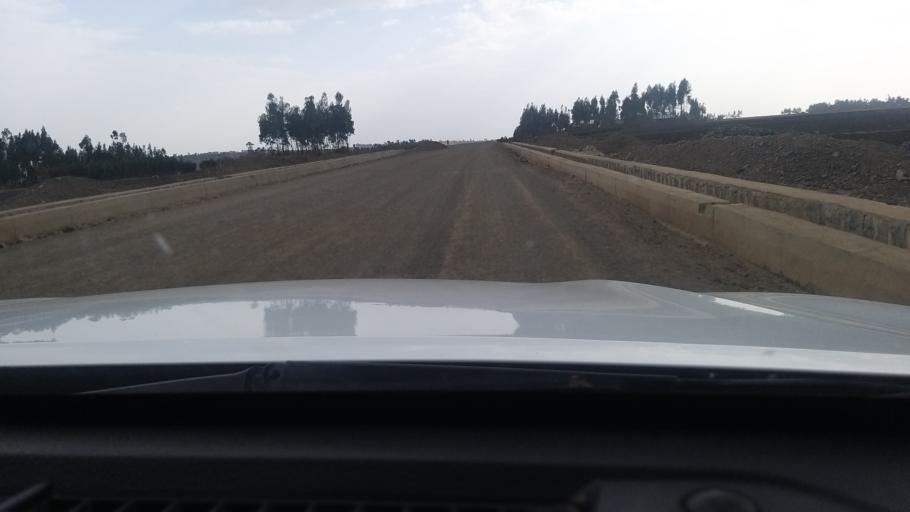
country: ET
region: Amhara
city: Were Ilu
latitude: 10.4535
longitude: 39.2113
